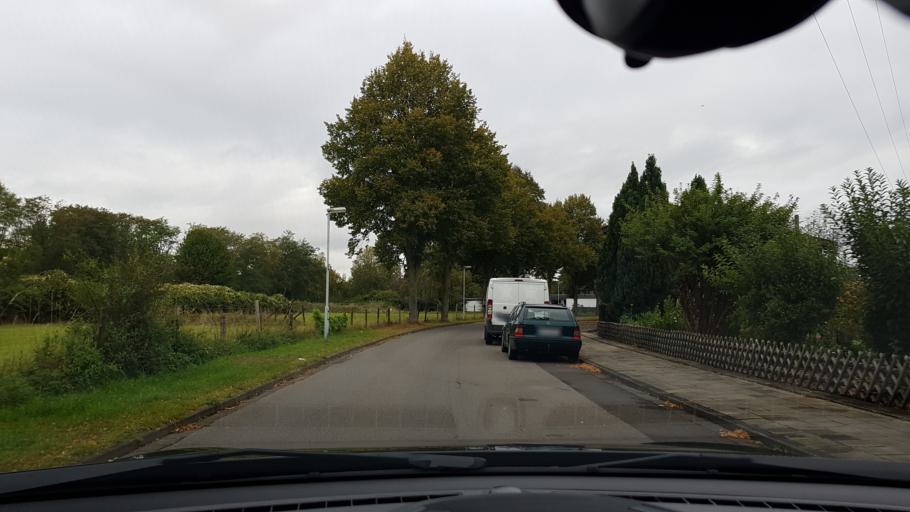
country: DE
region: North Rhine-Westphalia
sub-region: Regierungsbezirk Koln
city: Bergheim
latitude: 50.9800
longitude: 6.6636
